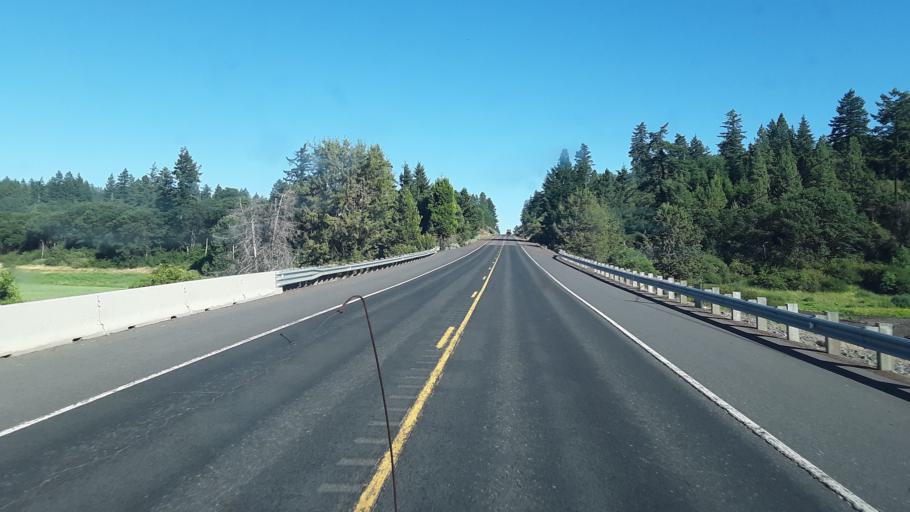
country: US
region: Oregon
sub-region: Klamath County
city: Klamath Falls
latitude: 42.2843
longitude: -121.9193
